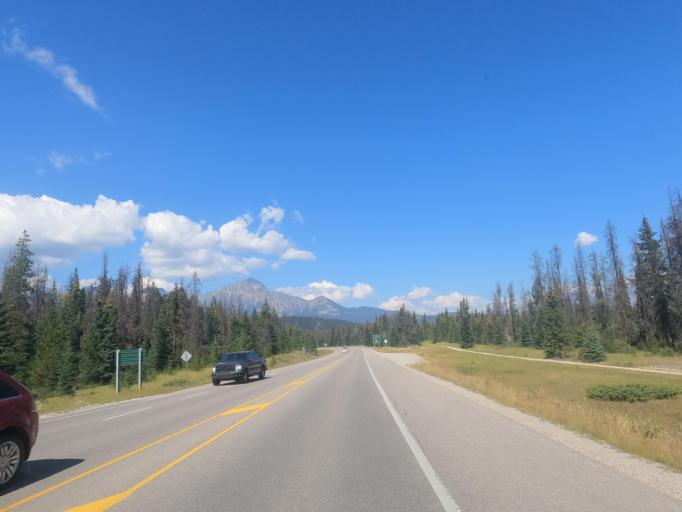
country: CA
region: Alberta
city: Jasper Park Lodge
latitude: 52.8554
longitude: -118.0781
